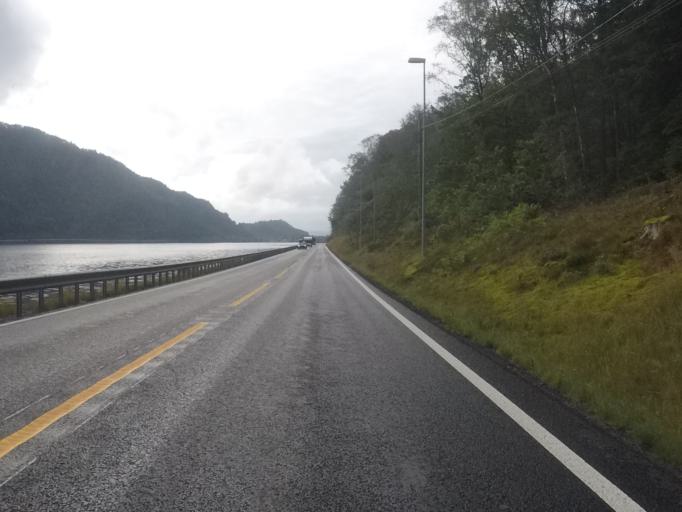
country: NO
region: Rogaland
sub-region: Lund
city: Moi
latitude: 58.4875
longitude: 6.5038
